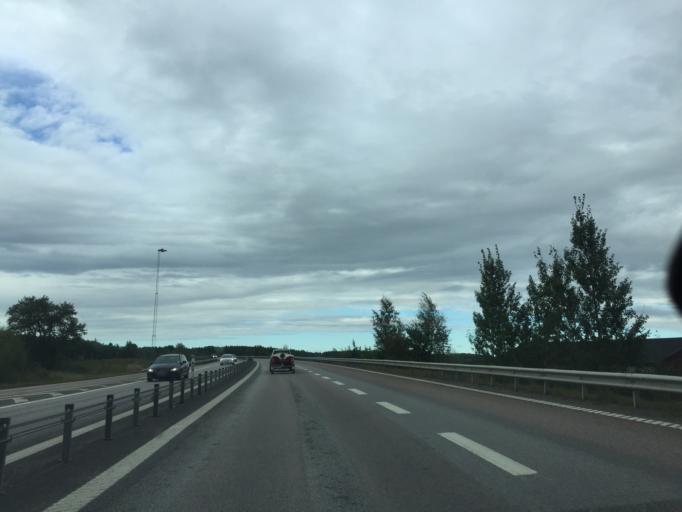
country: SE
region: Soedermanland
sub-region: Eskilstuna Kommun
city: Hallbybrunn
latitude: 59.4061
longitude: 16.4159
